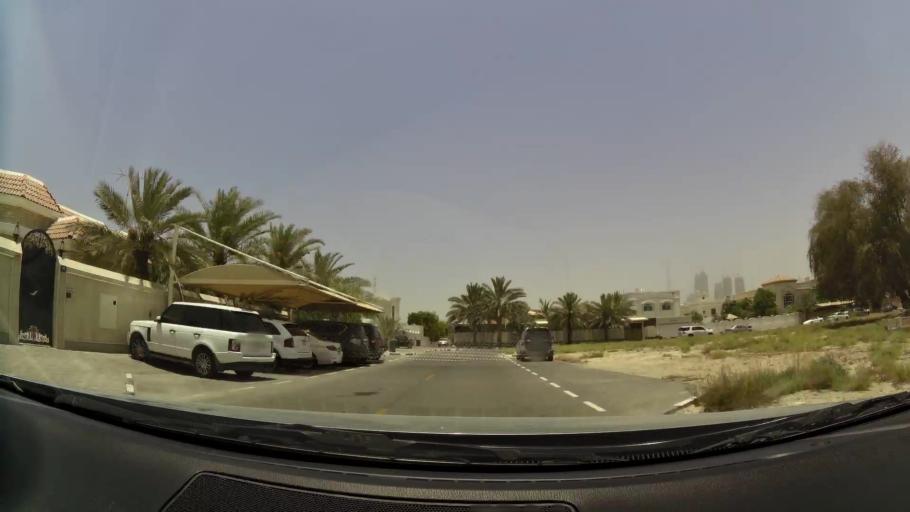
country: AE
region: Dubai
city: Dubai
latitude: 25.1748
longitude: 55.2363
